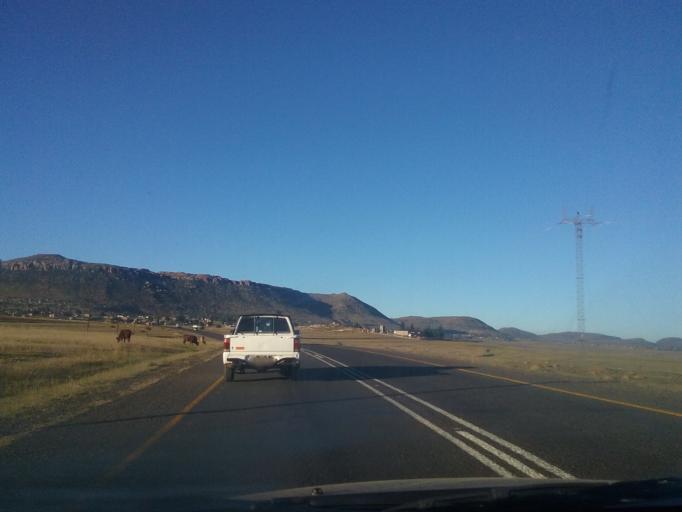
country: LS
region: Mohale's Hoek District
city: Mohale's Hoek
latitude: -30.1607
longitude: 27.4374
